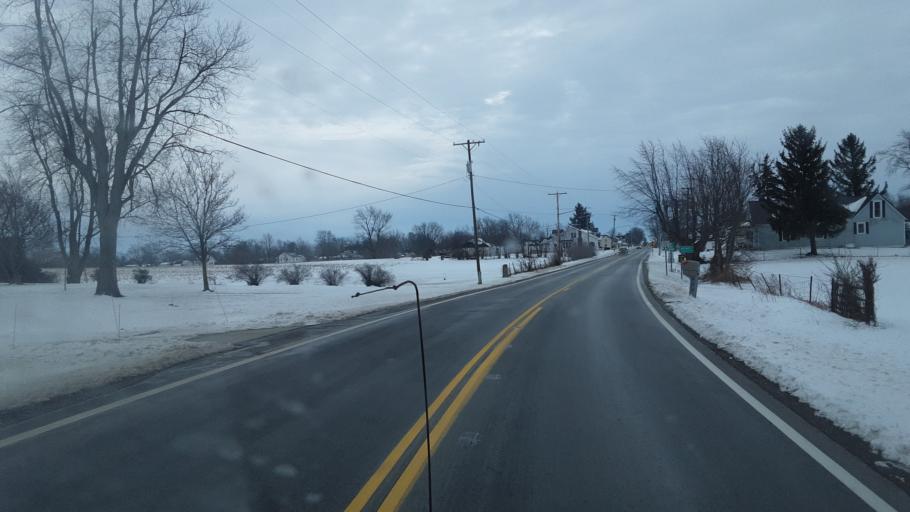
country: US
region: Ohio
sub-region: Madison County
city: Bethel
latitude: 39.7375
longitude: -83.4767
